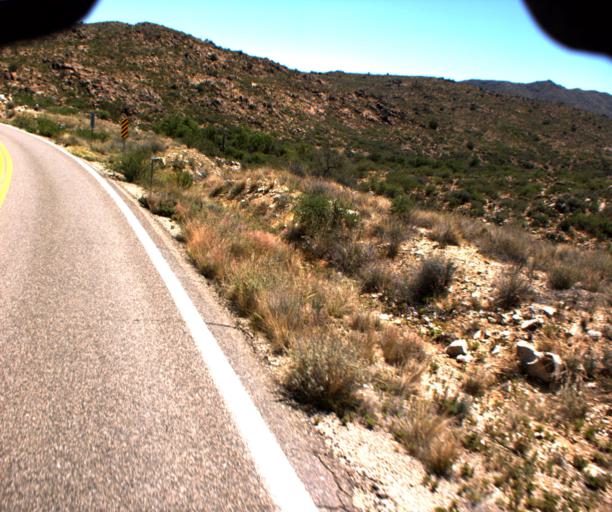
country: US
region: Arizona
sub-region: Yavapai County
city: Bagdad
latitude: 34.5249
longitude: -113.1271
